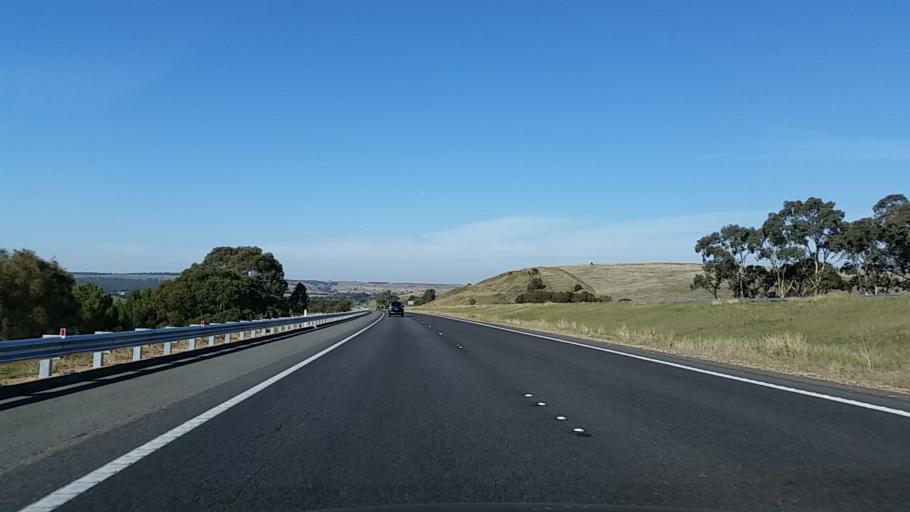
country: AU
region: South Australia
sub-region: Mount Barker
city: Callington
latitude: -35.1207
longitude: 139.0196
